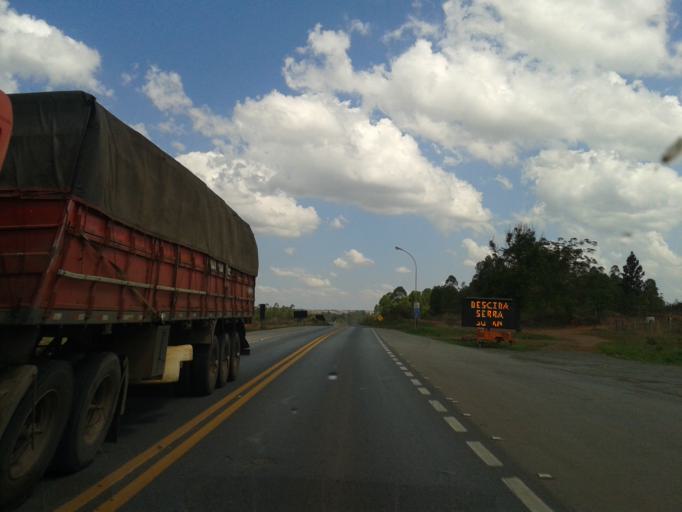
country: BR
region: Minas Gerais
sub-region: Campos Altos
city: Campos Altos
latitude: -19.6770
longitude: -46.0434
